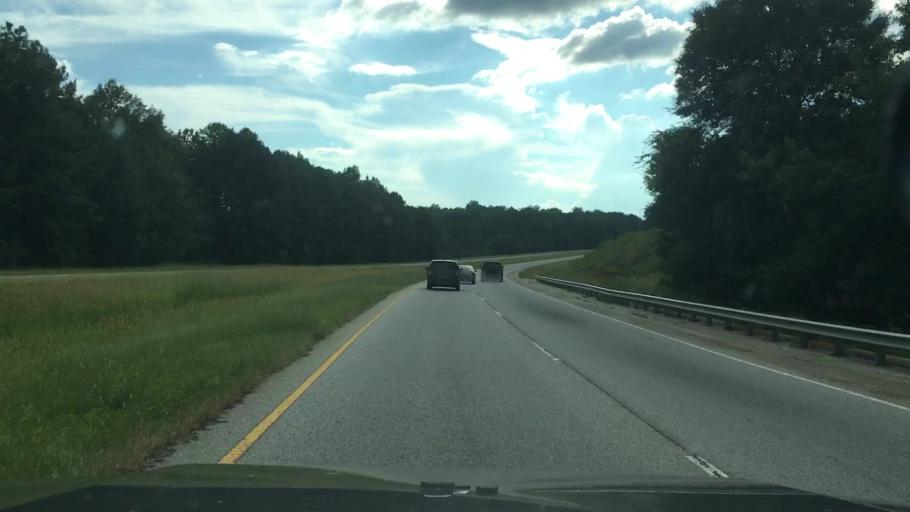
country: US
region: Georgia
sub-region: Spalding County
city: East Griffin
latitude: 33.2371
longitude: -84.1713
